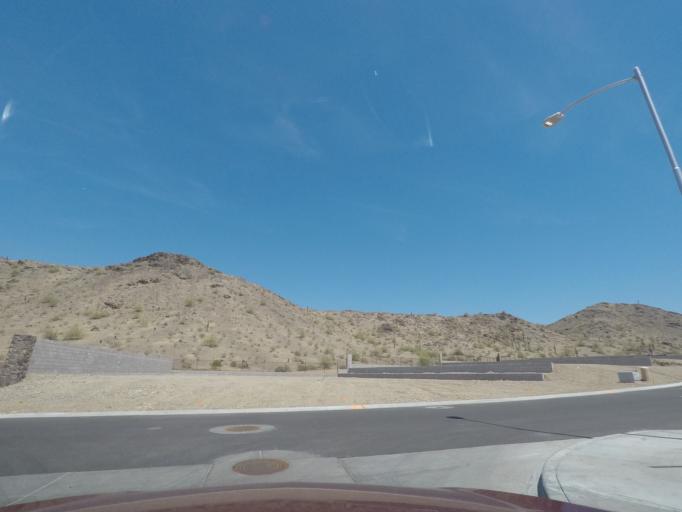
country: US
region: Arizona
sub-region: Maricopa County
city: Laveen
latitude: 33.3022
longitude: -112.1315
